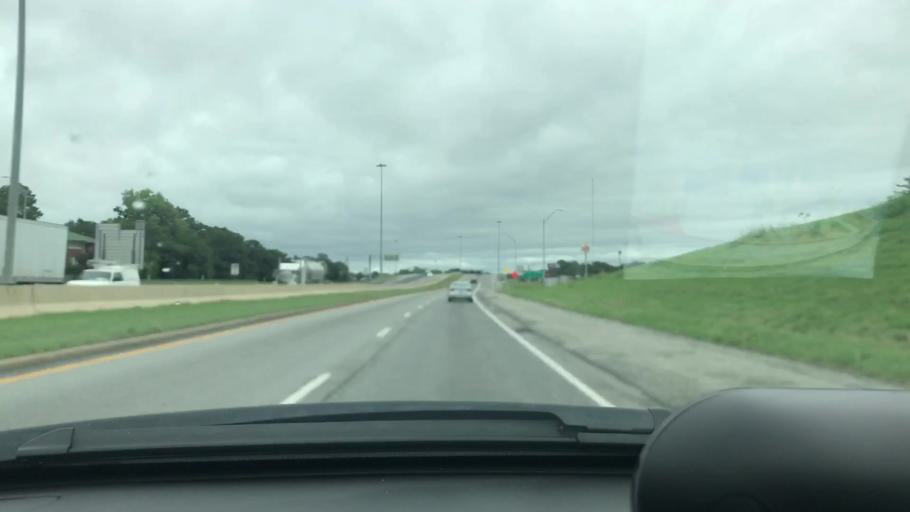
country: US
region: Texas
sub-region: Grayson County
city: Sherman
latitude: 33.6432
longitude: -96.6145
